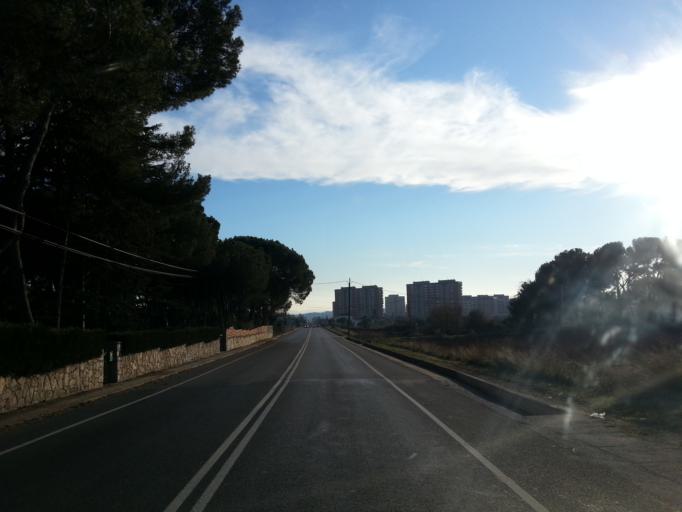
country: ES
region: Catalonia
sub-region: Provincia de Barcelona
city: Matadepera
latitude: 41.5888
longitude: 2.0190
